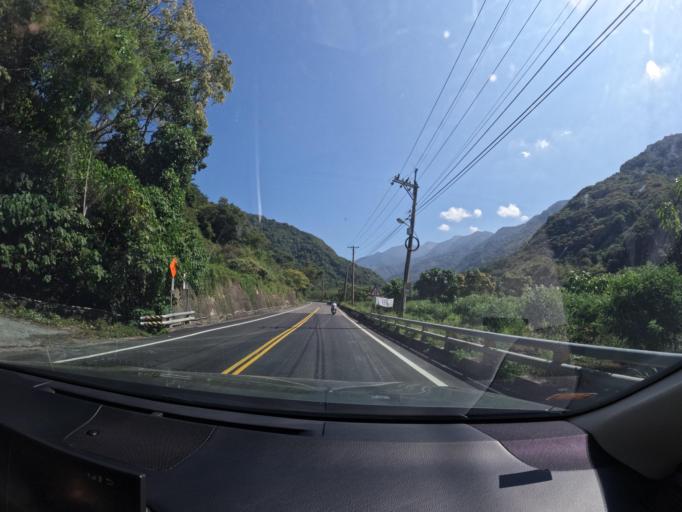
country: TW
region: Taiwan
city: Yujing
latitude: 23.1386
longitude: 120.7391
